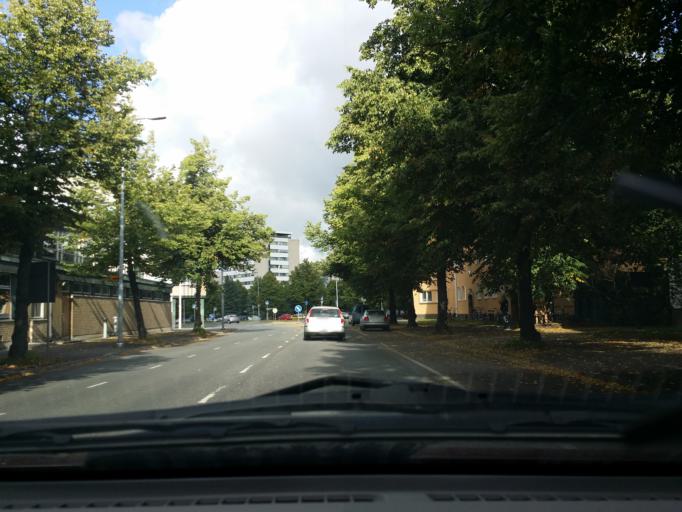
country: FI
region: Satakunta
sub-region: Pori
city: Pori
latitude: 61.4813
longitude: 21.7868
